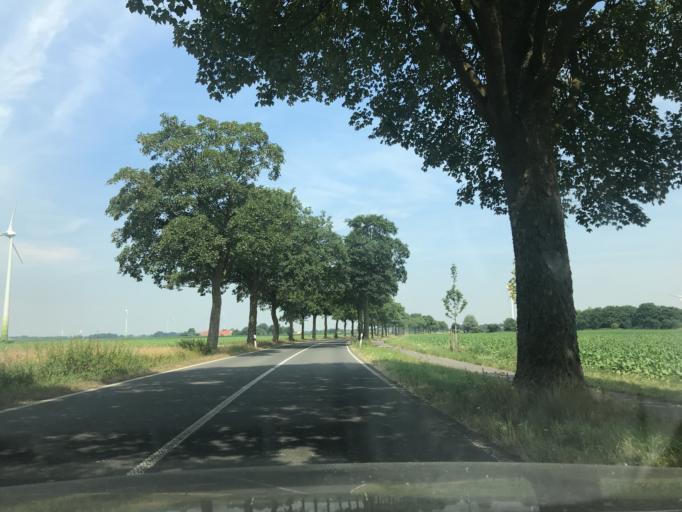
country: DE
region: North Rhine-Westphalia
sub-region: Regierungsbezirk Dusseldorf
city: Rheurdt
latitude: 51.4562
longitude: 6.4170
